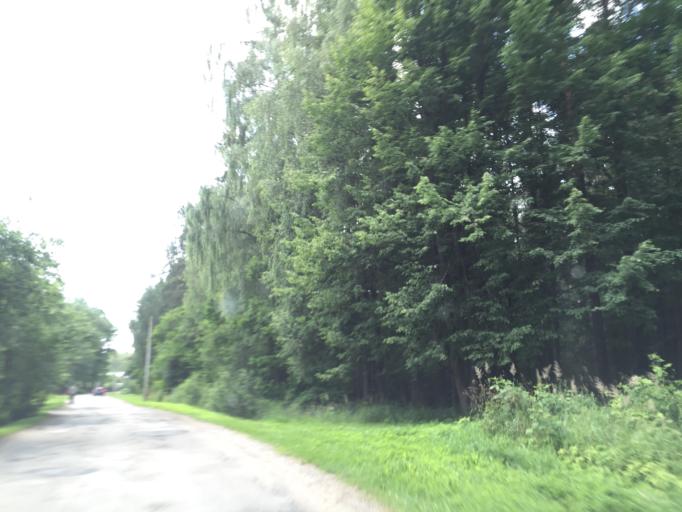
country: LV
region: Ozolnieku
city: Ozolnieki
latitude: 56.6913
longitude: 23.7637
